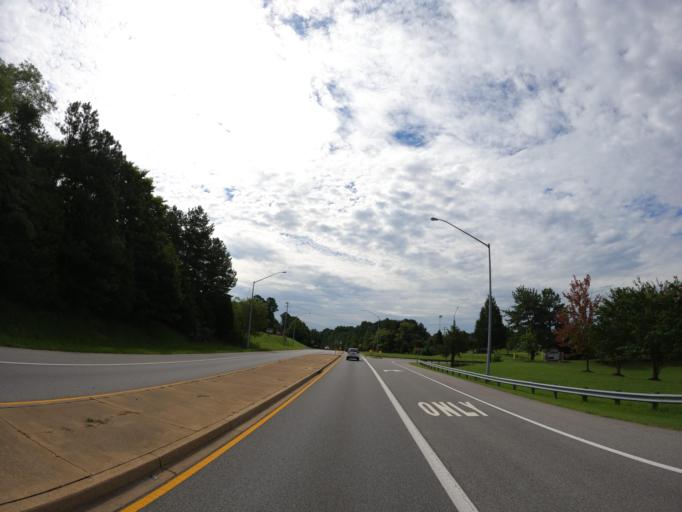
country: US
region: Maryland
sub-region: Saint Mary's County
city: Leonardtown
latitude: 38.2904
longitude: -76.6257
